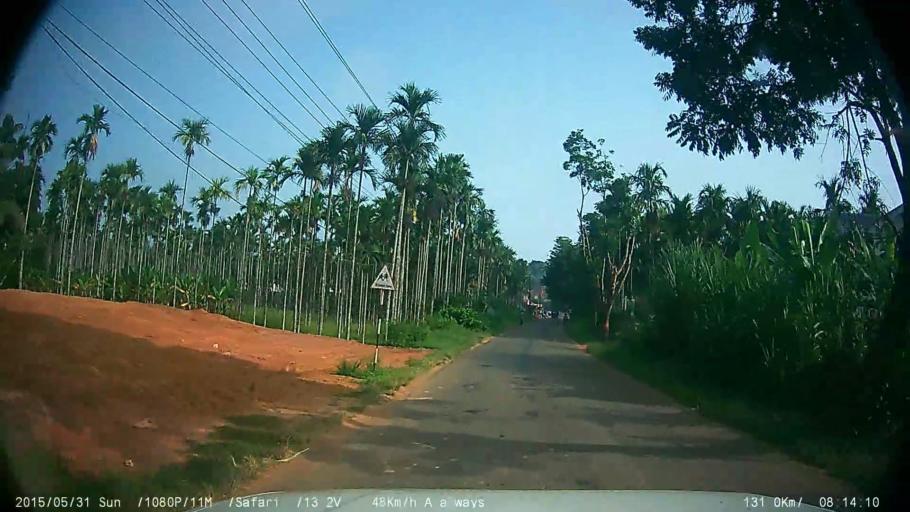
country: IN
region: Kerala
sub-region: Wayanad
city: Kalpetta
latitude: 11.6422
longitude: 76.0039
